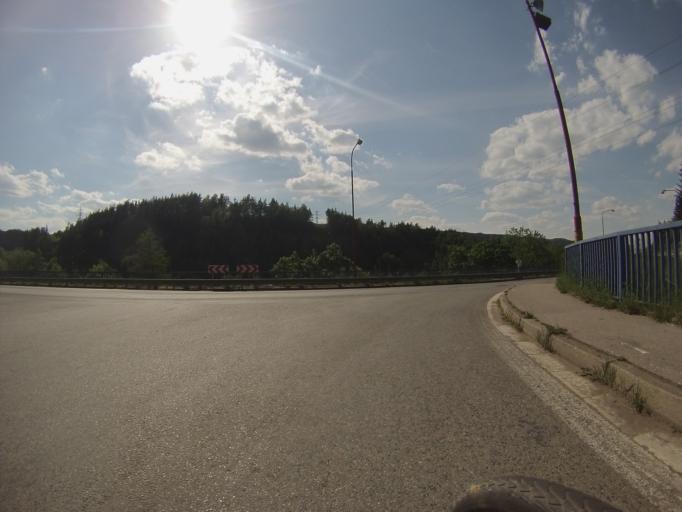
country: CZ
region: South Moravian
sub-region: Okres Blansko
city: Blansko
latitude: 49.3493
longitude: 16.6528
